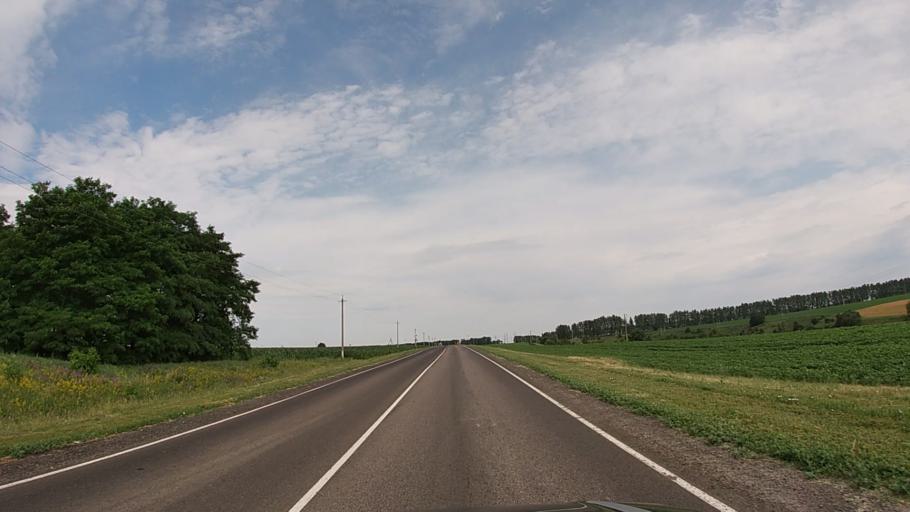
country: RU
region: Belgorod
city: Krasnaya Yaruga
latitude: 50.8316
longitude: 35.4928
